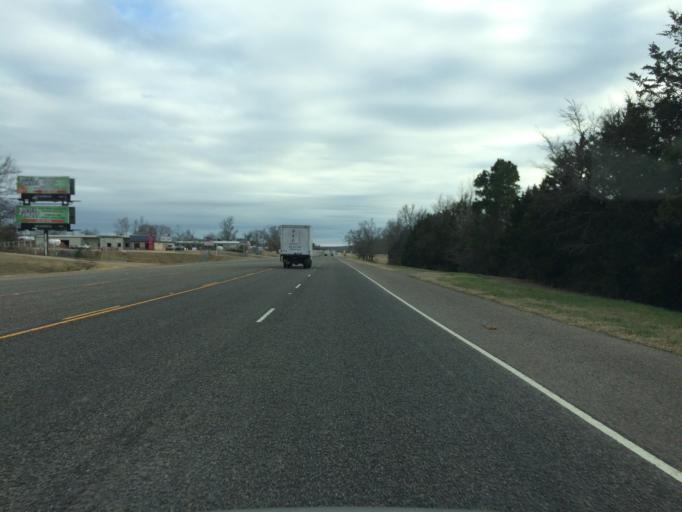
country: US
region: Texas
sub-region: Wood County
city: Mineola
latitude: 32.6451
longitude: -95.4899
